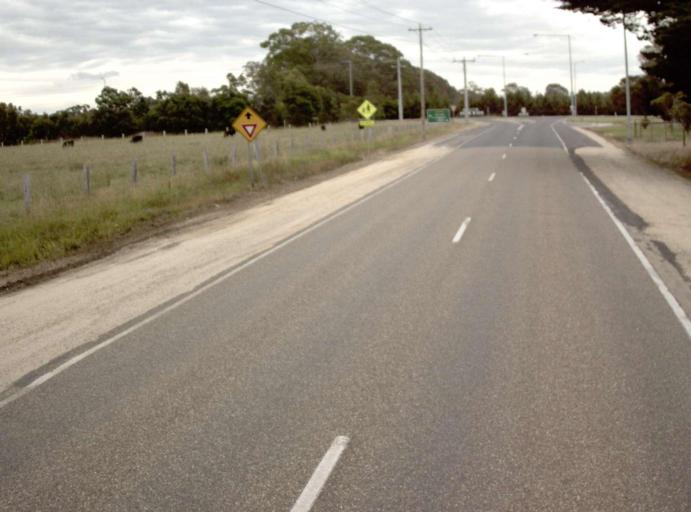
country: AU
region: Victoria
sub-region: Wellington
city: Sale
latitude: -38.1627
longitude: 147.0882
